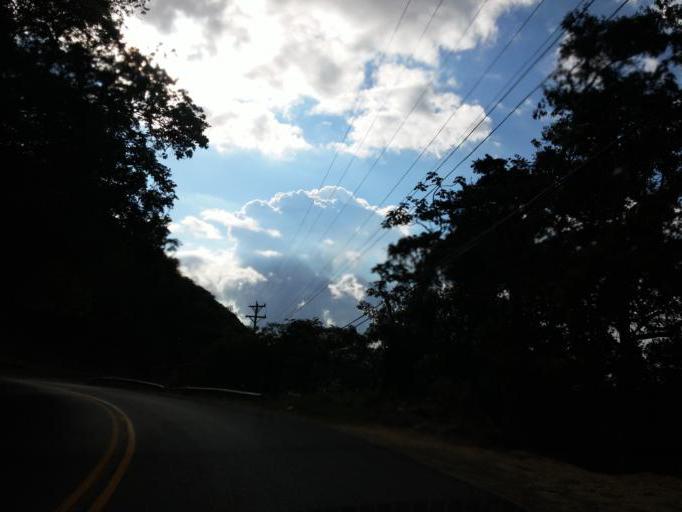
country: CR
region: San Jose
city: San Ignacio
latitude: 9.7975
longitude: -84.1335
